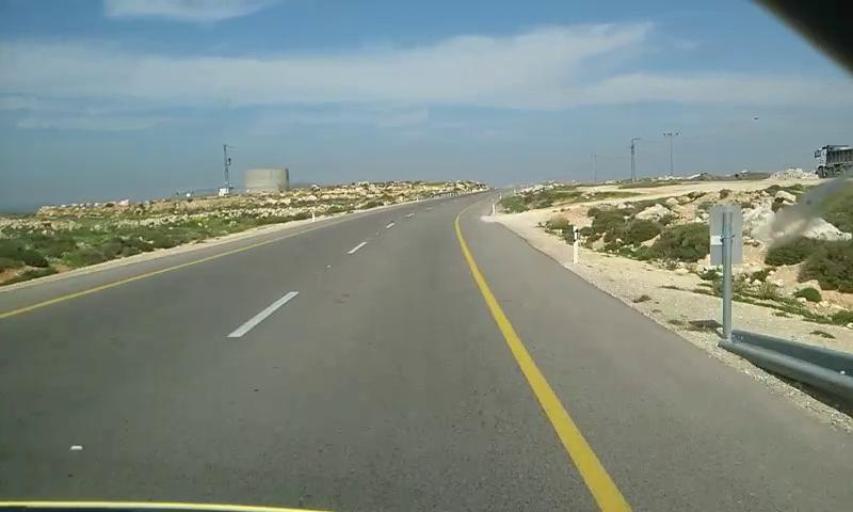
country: PS
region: West Bank
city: As Samu`
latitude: 31.3984
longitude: 35.0294
